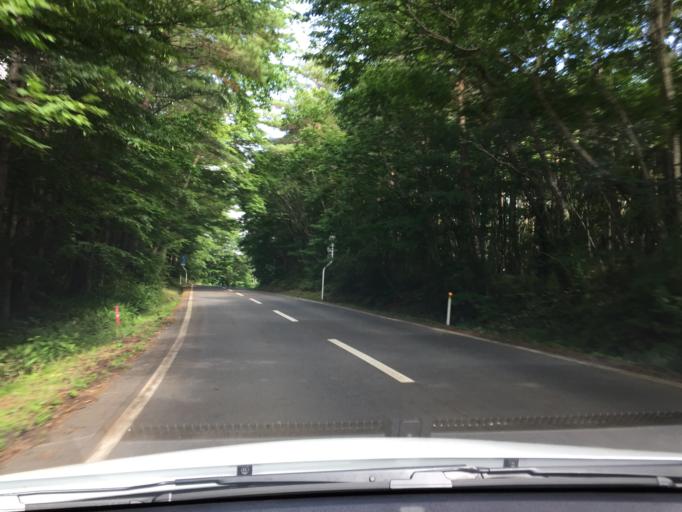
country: JP
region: Tochigi
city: Kuroiso
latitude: 37.2268
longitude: 140.0822
